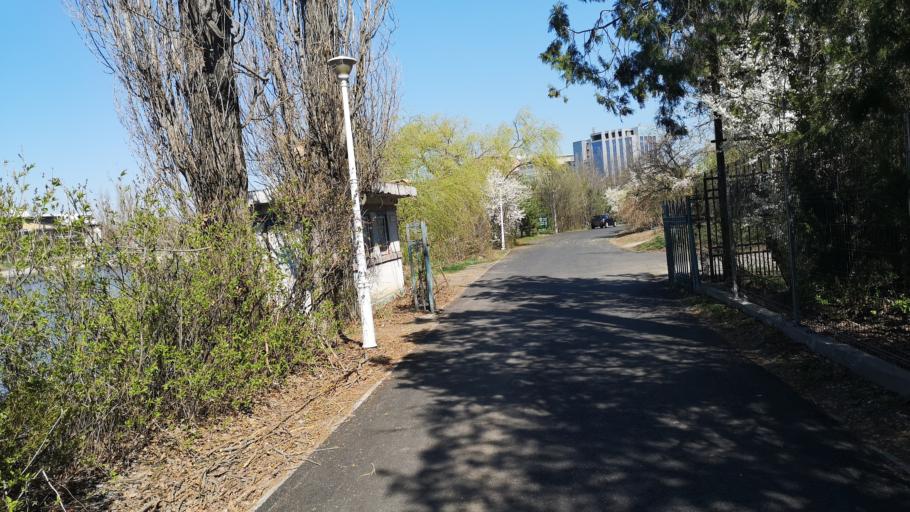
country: RO
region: Ilfov
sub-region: Comuna Otopeni
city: Otopeni
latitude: 44.4879
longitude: 26.0763
